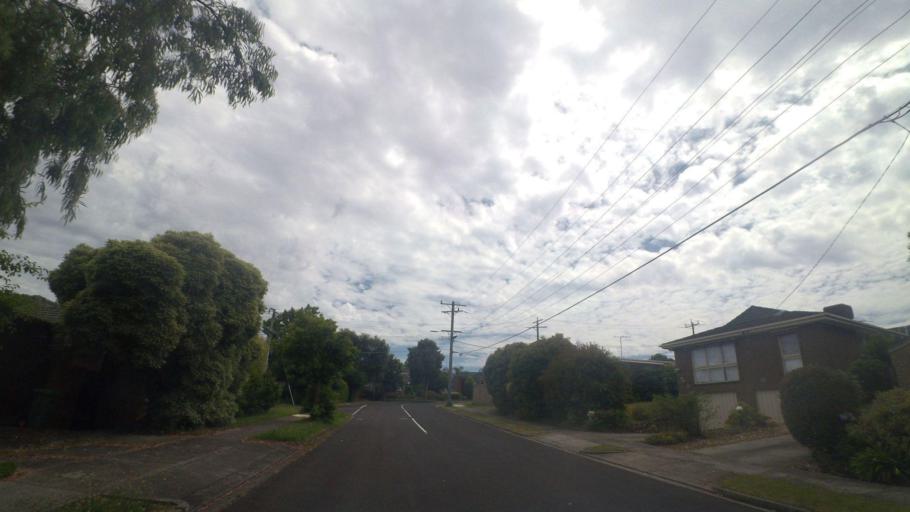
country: AU
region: Victoria
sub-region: Banyule
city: Viewbank
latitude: -37.7400
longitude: 145.0900
